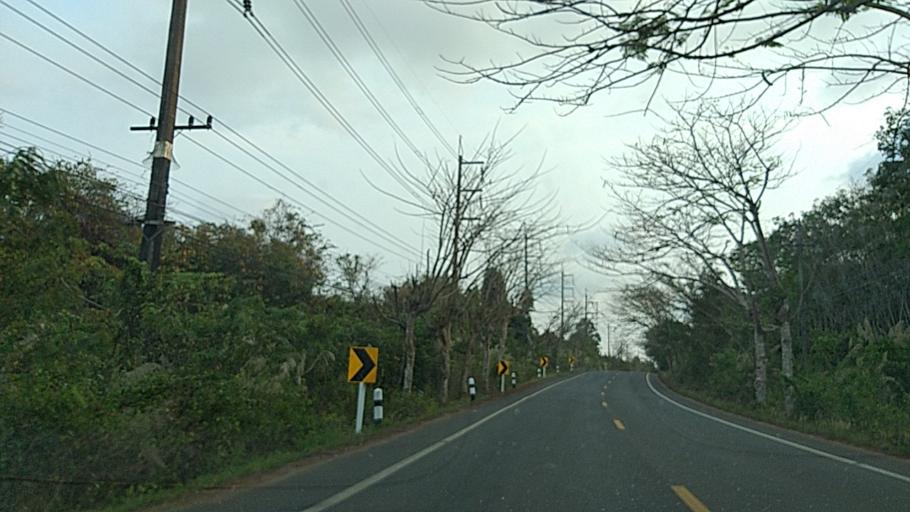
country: TH
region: Trat
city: Laem Ngop
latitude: 12.2698
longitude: 102.3057
